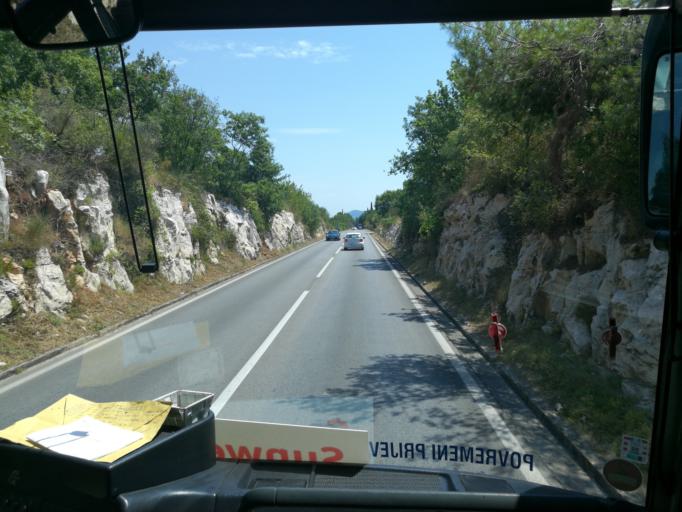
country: HR
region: Dubrovacko-Neretvanska
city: Jasenice
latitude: 42.5620
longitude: 18.2540
